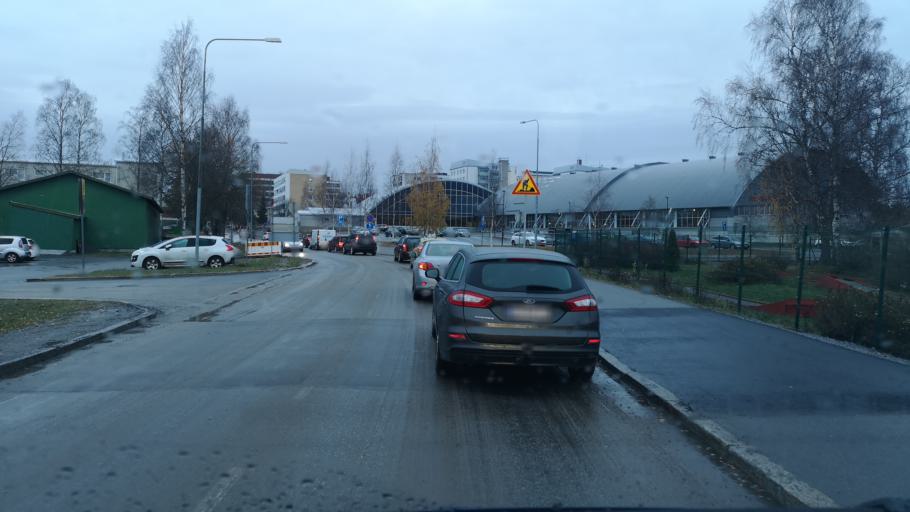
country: FI
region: Ostrobothnia
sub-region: Vaasa
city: Vaasa
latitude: 63.0851
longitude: 21.6201
